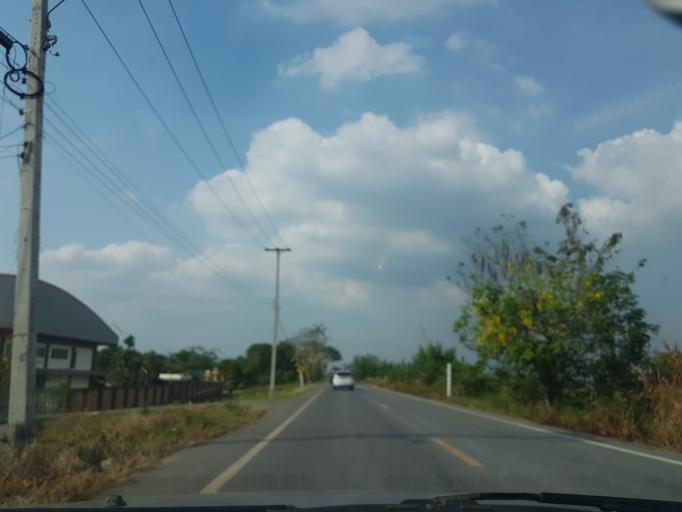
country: TH
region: Phra Nakhon Si Ayutthaya
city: Phachi
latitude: 14.4218
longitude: 100.7802
